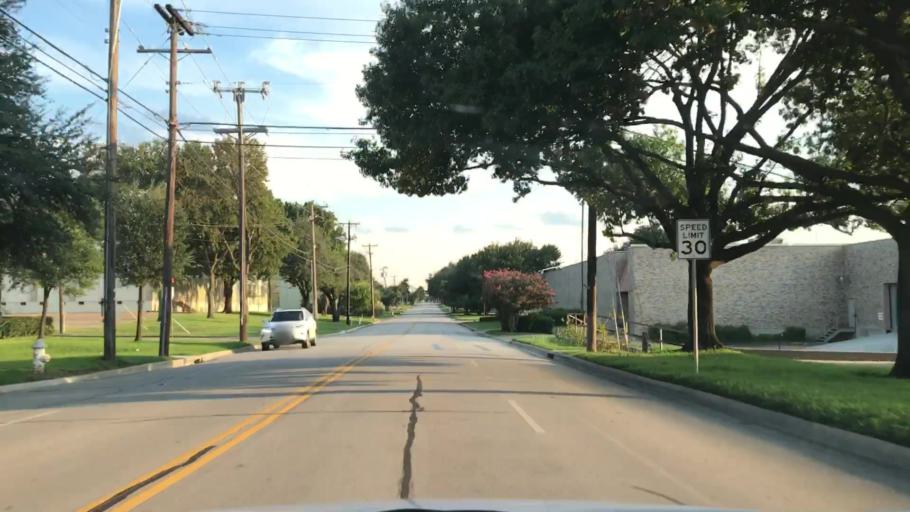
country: US
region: Texas
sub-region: Dallas County
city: Addison
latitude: 32.9383
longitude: -96.8305
